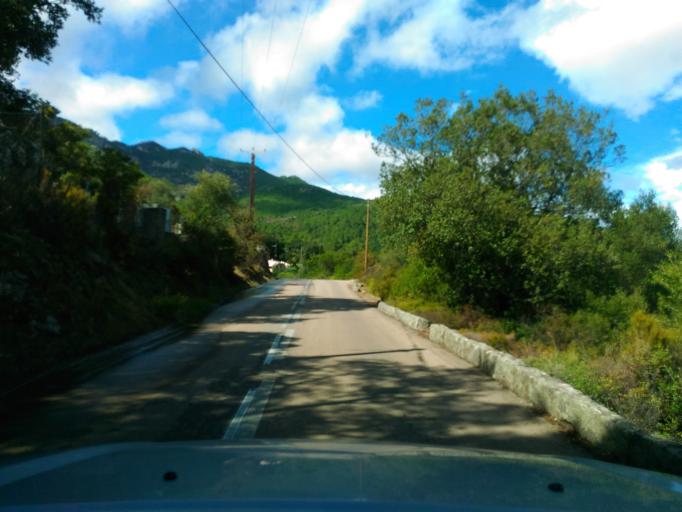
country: FR
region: Corsica
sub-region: Departement de la Corse-du-Sud
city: Porto-Vecchio
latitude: 41.7112
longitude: 9.3084
